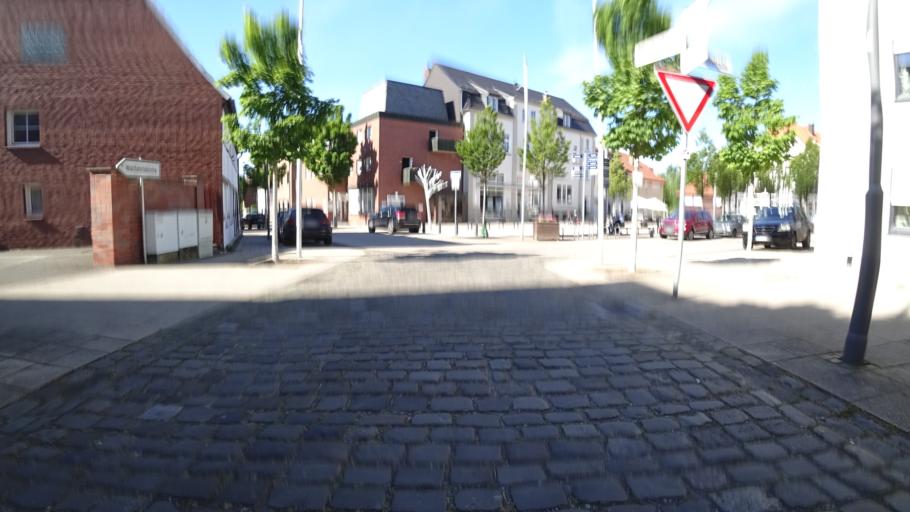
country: DE
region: North Rhine-Westphalia
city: Oelde
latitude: 51.8014
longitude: 8.2038
